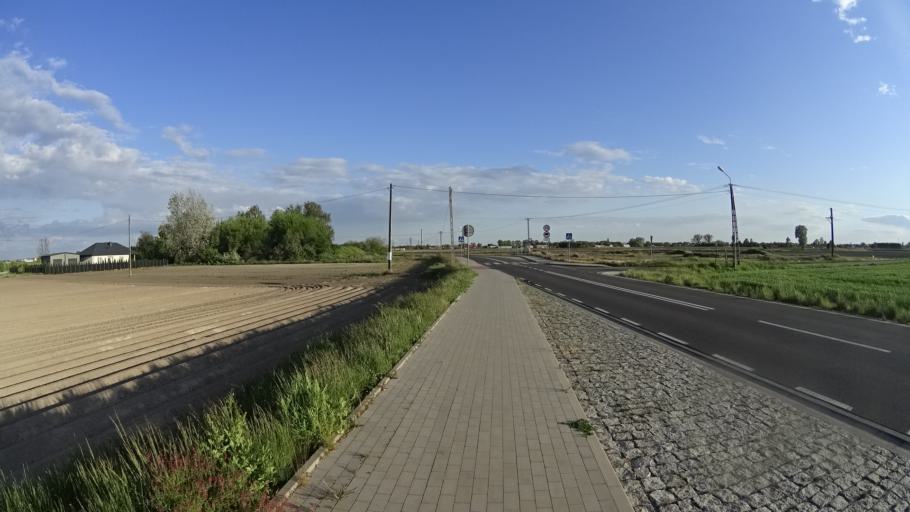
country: PL
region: Masovian Voivodeship
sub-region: Powiat warszawski zachodni
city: Jozefow
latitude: 52.2236
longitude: 20.7379
